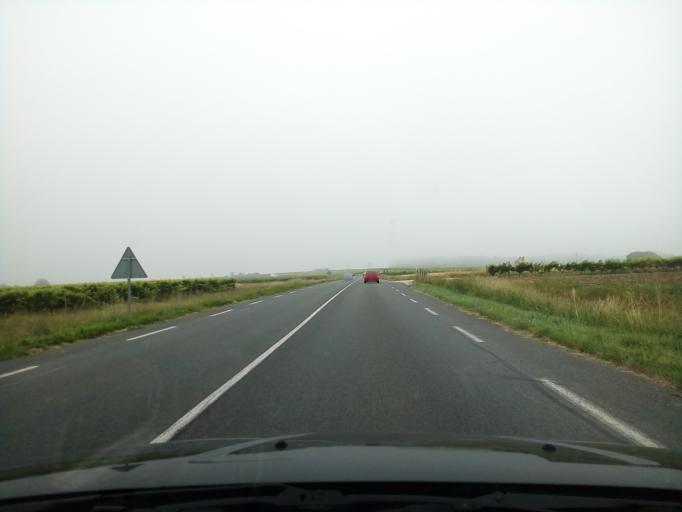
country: FR
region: Poitou-Charentes
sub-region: Departement de la Charente-Maritime
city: Cherac
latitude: 45.6912
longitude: -0.4092
